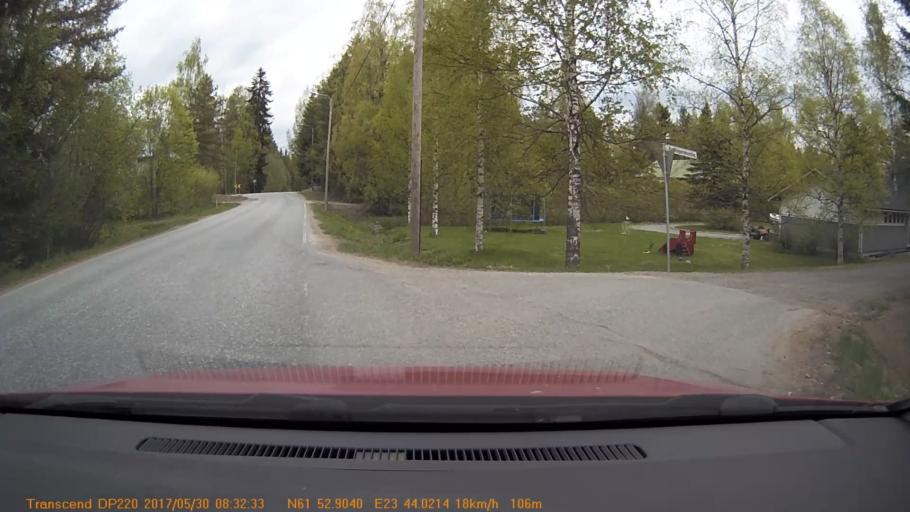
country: FI
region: Pirkanmaa
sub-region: Tampere
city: Kuru
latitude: 61.8817
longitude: 23.7337
